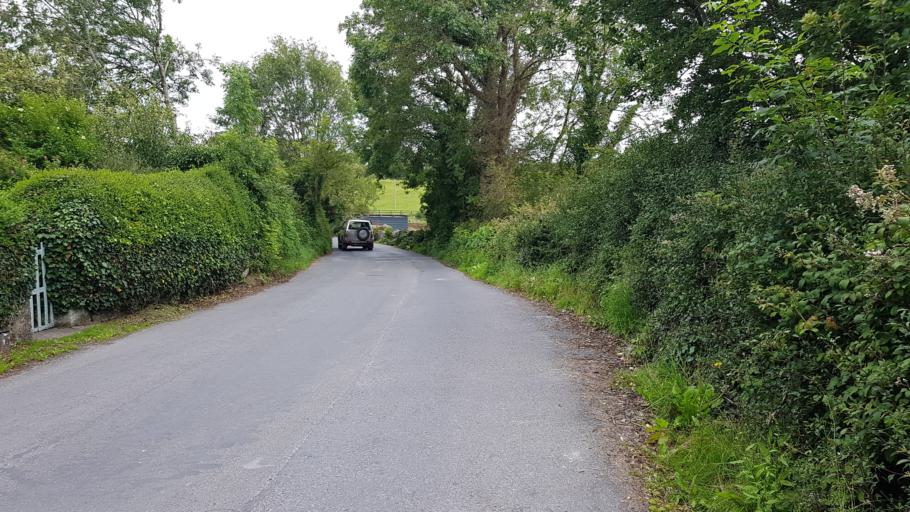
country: IE
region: Connaught
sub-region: County Galway
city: Gaillimh
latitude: 53.2970
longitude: -9.0203
